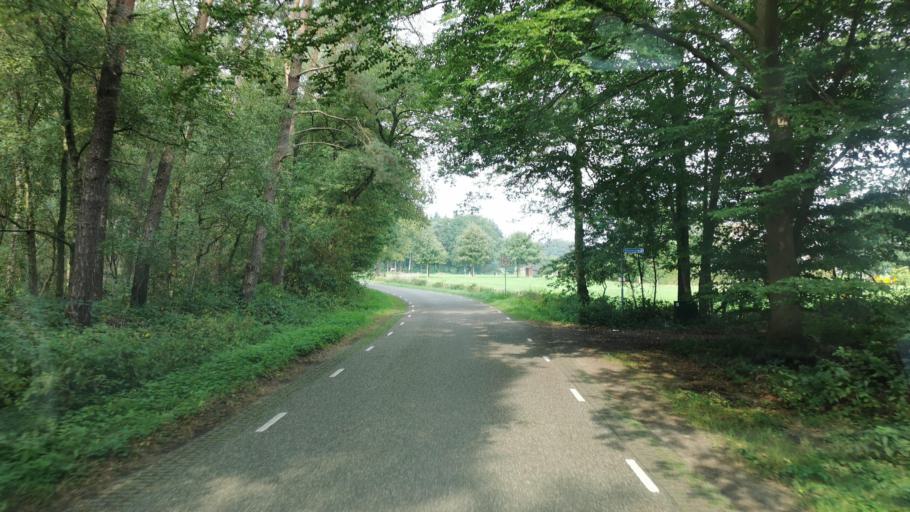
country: NL
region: Overijssel
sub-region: Gemeente Losser
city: Losser
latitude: 52.2890
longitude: 7.0202
